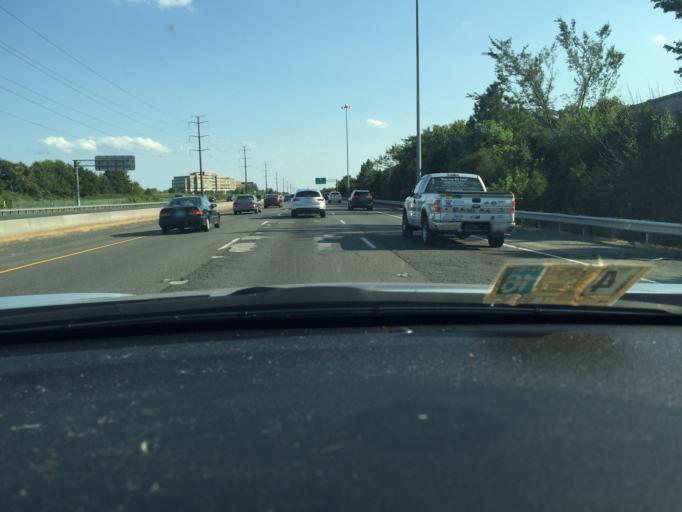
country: US
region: Virginia
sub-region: Fairfax County
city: Floris
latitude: 38.9430
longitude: -77.4298
